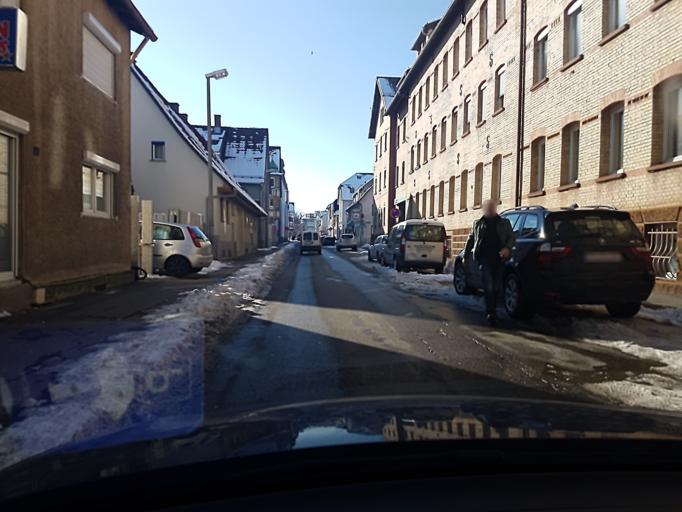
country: DE
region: Baden-Wuerttemberg
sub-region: Freiburg Region
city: Dauchingen
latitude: 48.0630
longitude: 8.5301
